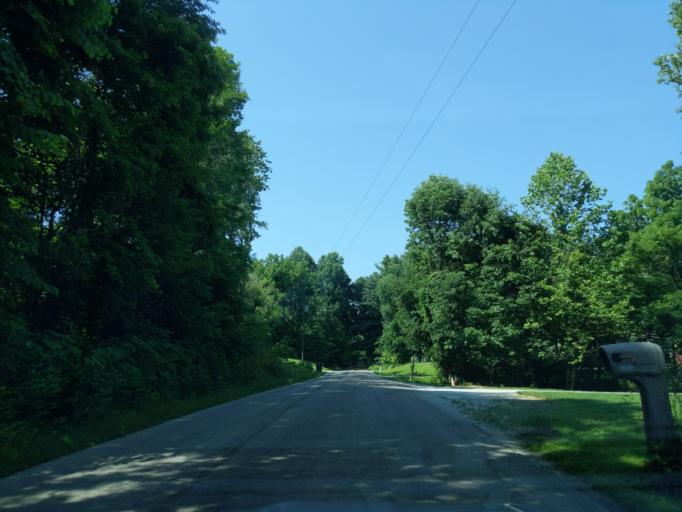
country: US
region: Indiana
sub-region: Ripley County
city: Osgood
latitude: 39.1275
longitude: -85.3413
